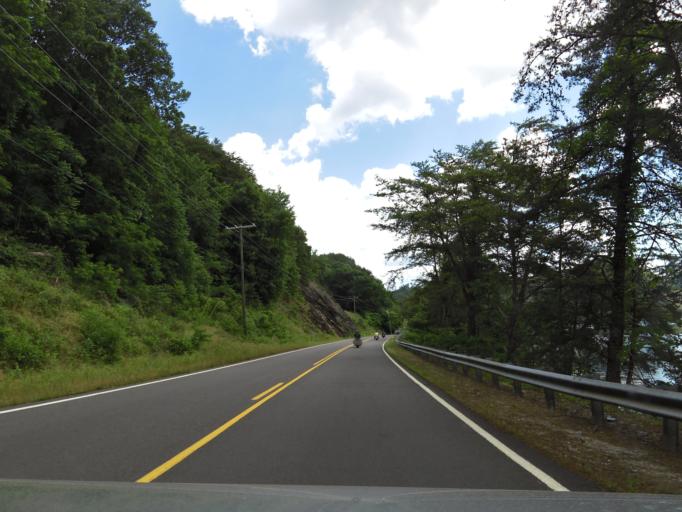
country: US
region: Tennessee
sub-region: Loudon County
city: Greenback
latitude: 35.5543
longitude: -84.0162
